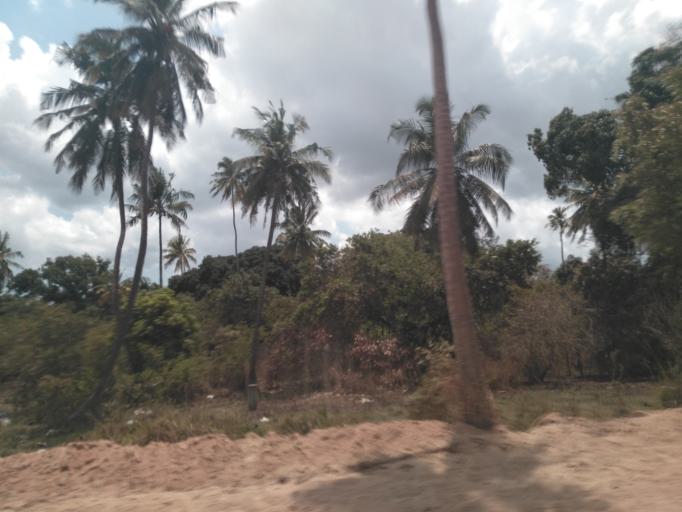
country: TZ
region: Dar es Salaam
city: Dar es Salaam
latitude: -6.8664
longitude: 39.3290
